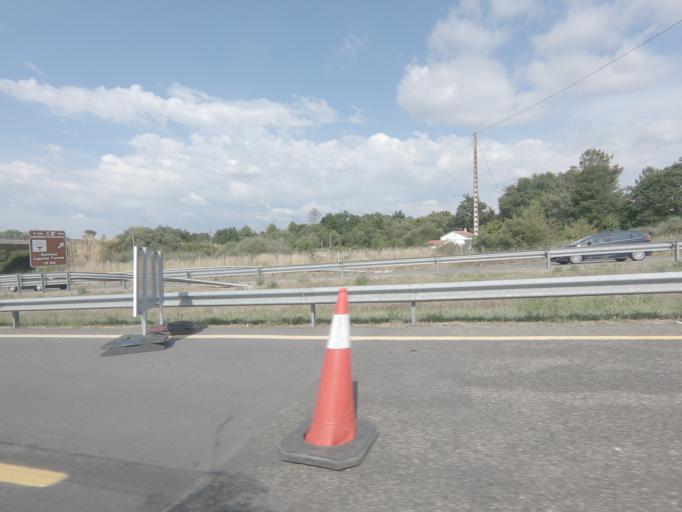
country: ES
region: Galicia
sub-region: Provincia de Ourense
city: Taboadela
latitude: 42.2557
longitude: -7.8690
